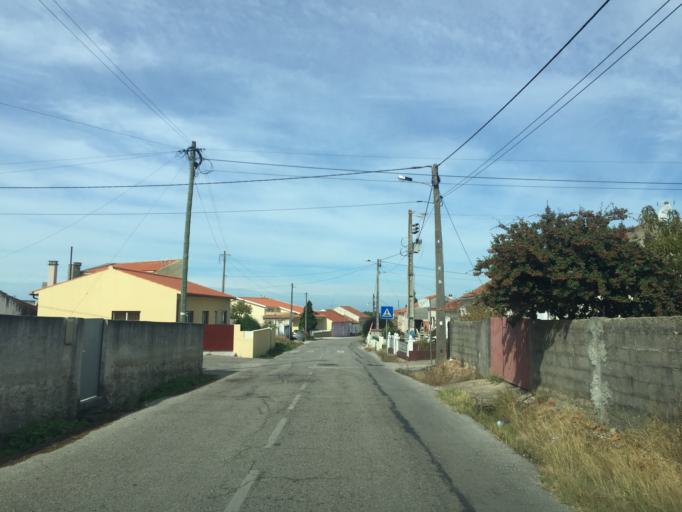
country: PT
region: Coimbra
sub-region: Figueira da Foz
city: Lavos
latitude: 40.0810
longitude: -8.8298
